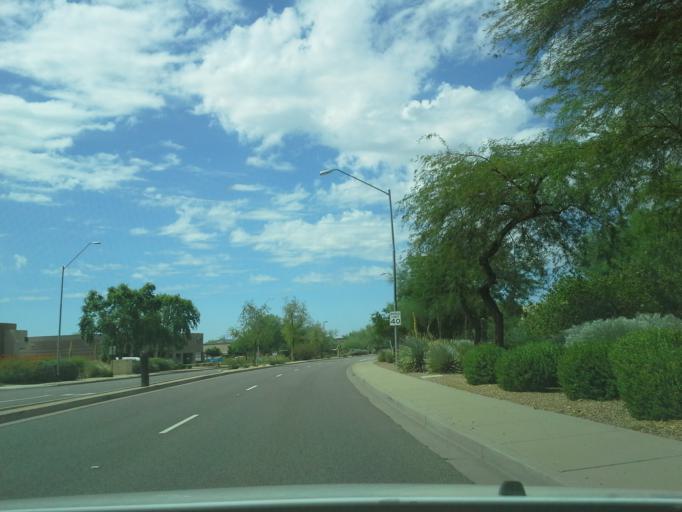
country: US
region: Arizona
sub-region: Maricopa County
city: Paradise Valley
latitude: 33.6327
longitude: -111.9087
